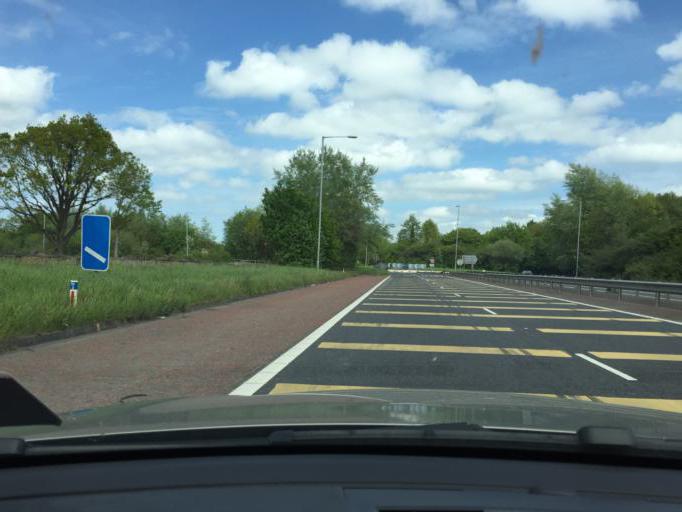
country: GB
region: Northern Ireland
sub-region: Craigavon District
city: Craigavon
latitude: 54.4614
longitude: -6.4186
